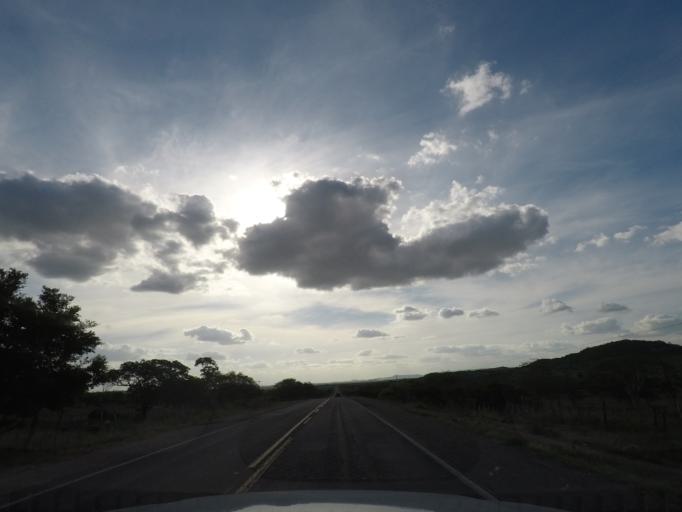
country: BR
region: Bahia
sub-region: Anguera
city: Anguera
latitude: -12.1840
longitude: -39.4713
